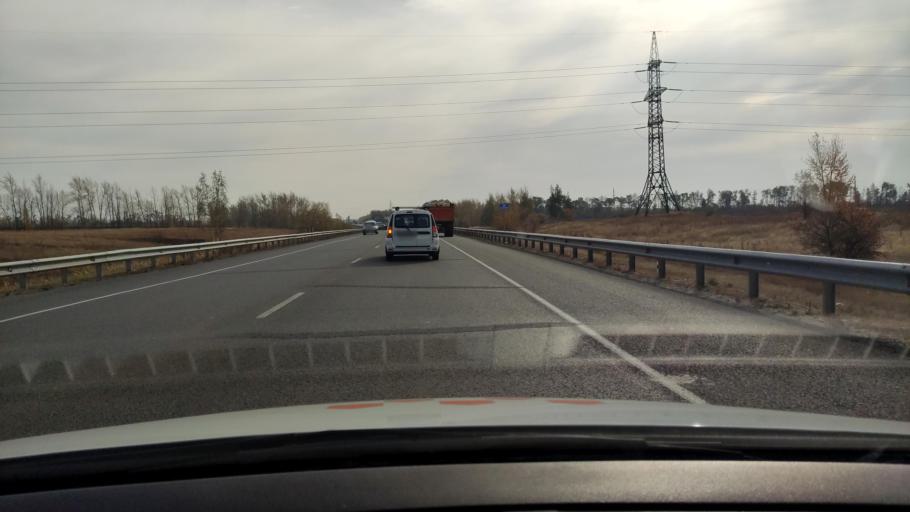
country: RU
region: Voronezj
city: Novaya Usman'
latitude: 51.6972
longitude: 39.4344
